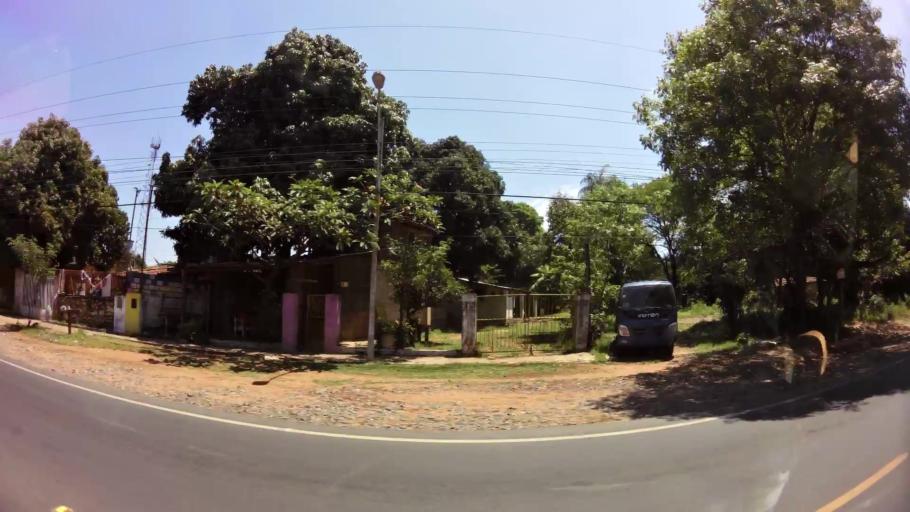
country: PY
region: Central
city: San Antonio
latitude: -25.4077
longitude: -57.5452
